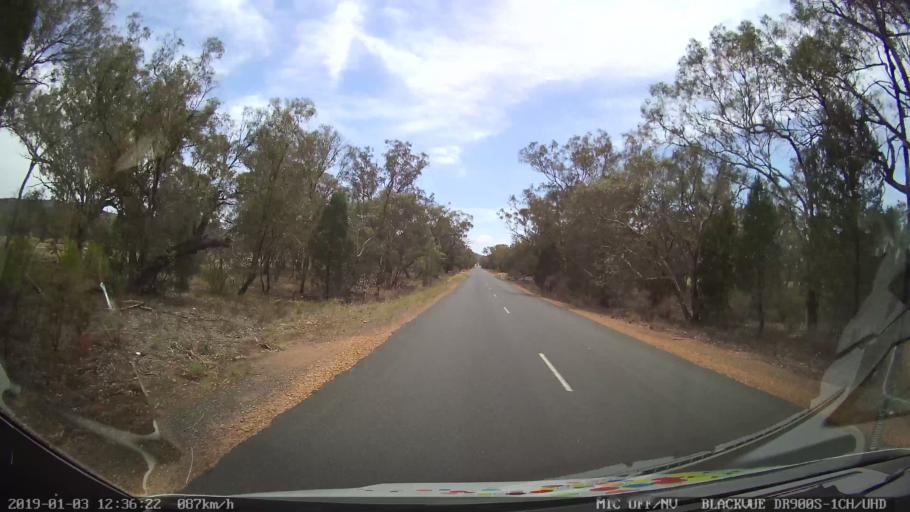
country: AU
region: New South Wales
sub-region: Weddin
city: Grenfell
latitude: -33.8558
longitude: 148.1765
